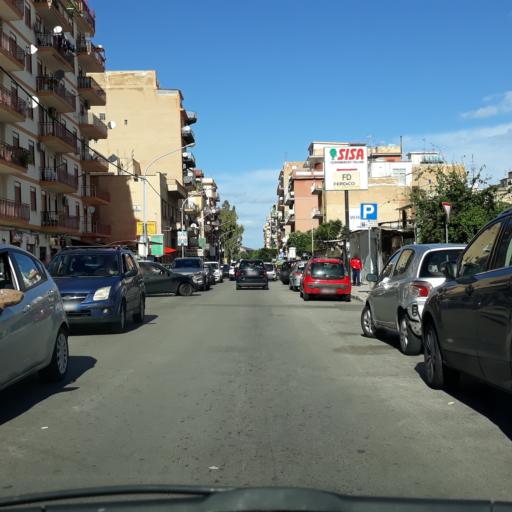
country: IT
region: Sicily
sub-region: Palermo
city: Palermo
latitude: 38.1510
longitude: 13.3707
